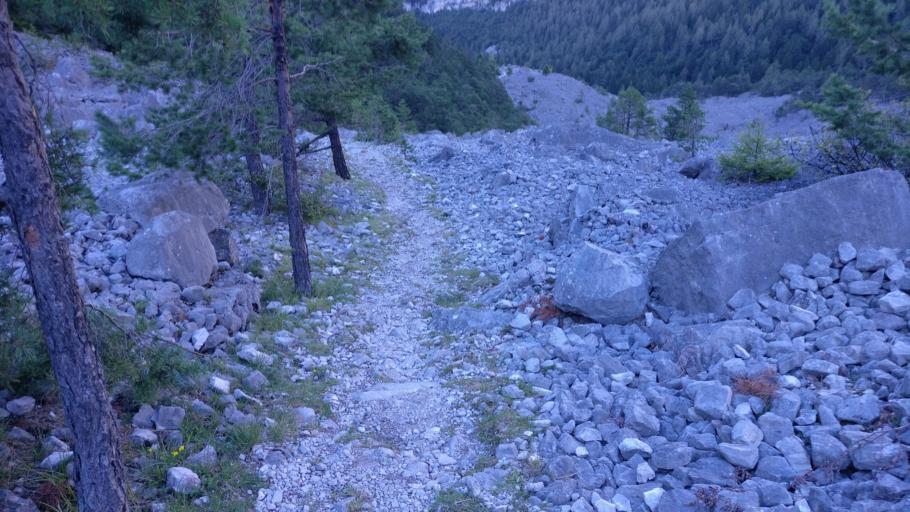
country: IT
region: Trentino-Alto Adige
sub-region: Provincia di Trento
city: Terres
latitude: 46.2836
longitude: 10.9669
